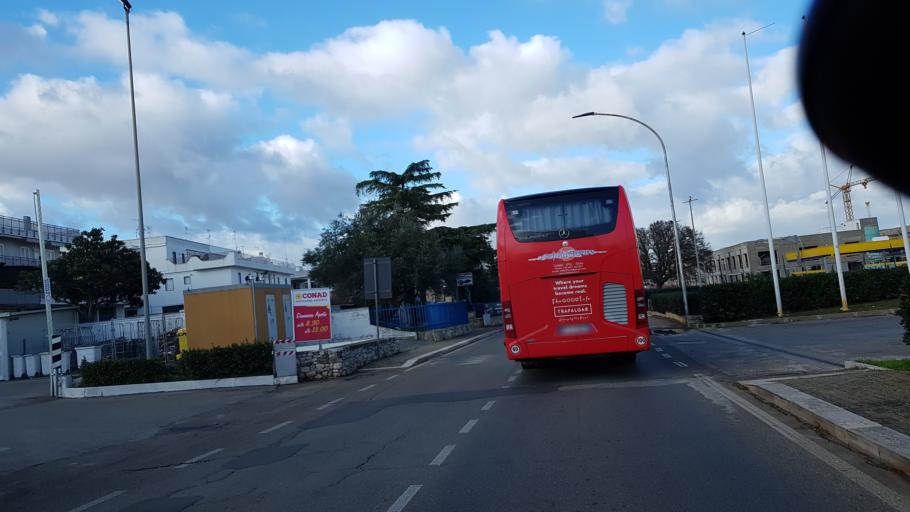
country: IT
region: Apulia
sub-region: Provincia di Bari
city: Alberobello
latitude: 40.7859
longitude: 17.2446
